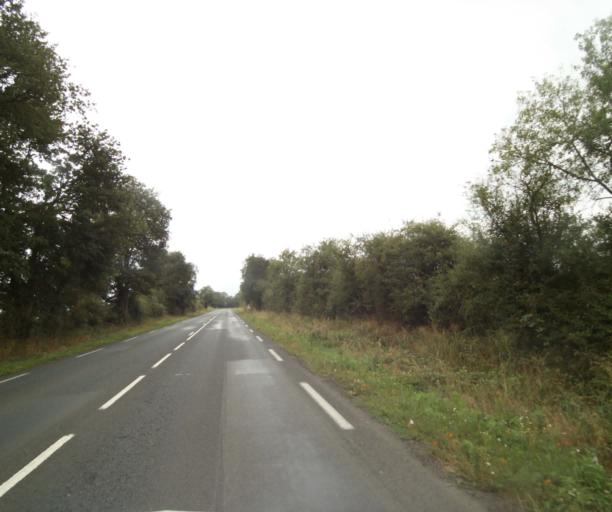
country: FR
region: Pays de la Loire
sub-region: Departement de la Sarthe
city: Vion
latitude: 47.8377
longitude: -0.2556
